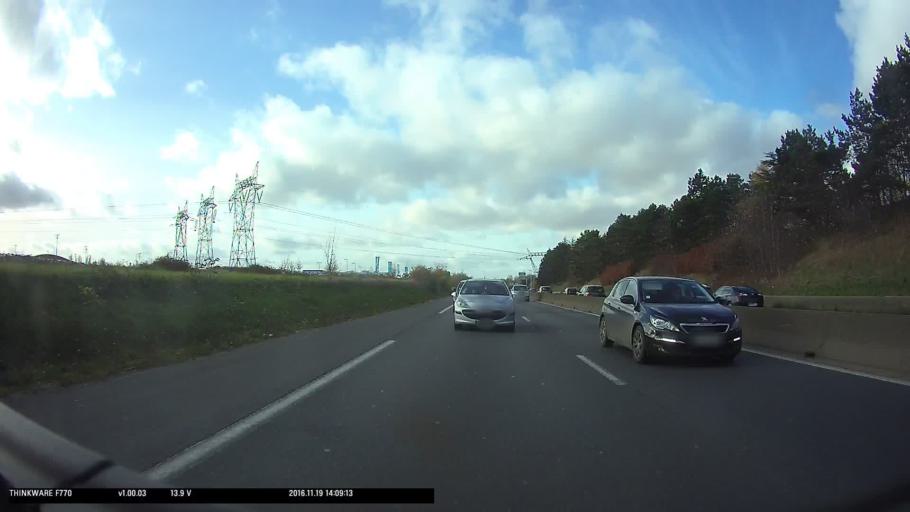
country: FR
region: Ile-de-France
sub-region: Departement du Val-d'Oise
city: Osny
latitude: 49.0553
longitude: 2.0539
